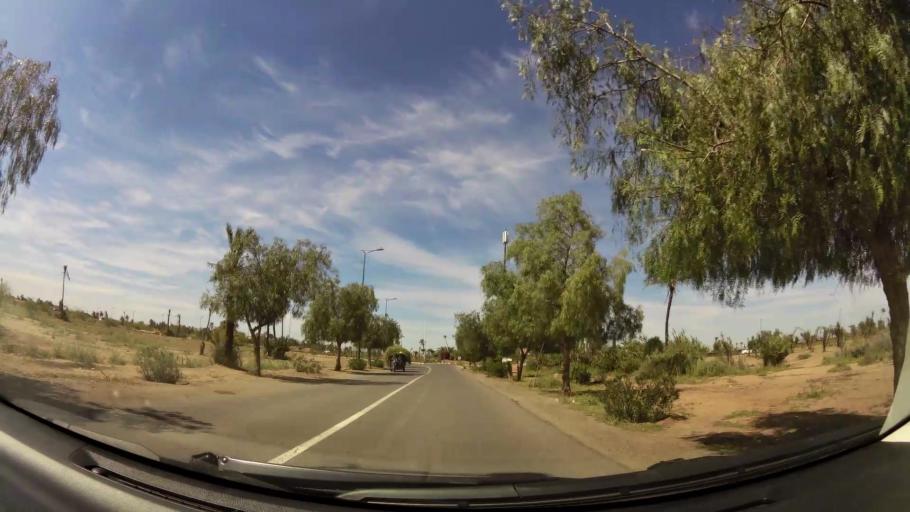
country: MA
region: Marrakech-Tensift-Al Haouz
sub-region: Marrakech
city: Marrakesh
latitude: 31.6156
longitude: -7.9539
